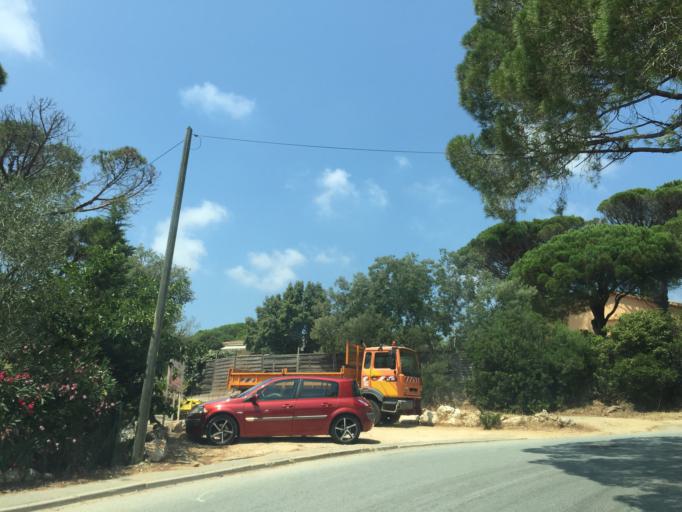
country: FR
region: Provence-Alpes-Cote d'Azur
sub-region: Departement du Var
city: Sainte-Maxime
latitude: 43.3446
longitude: 6.6768
